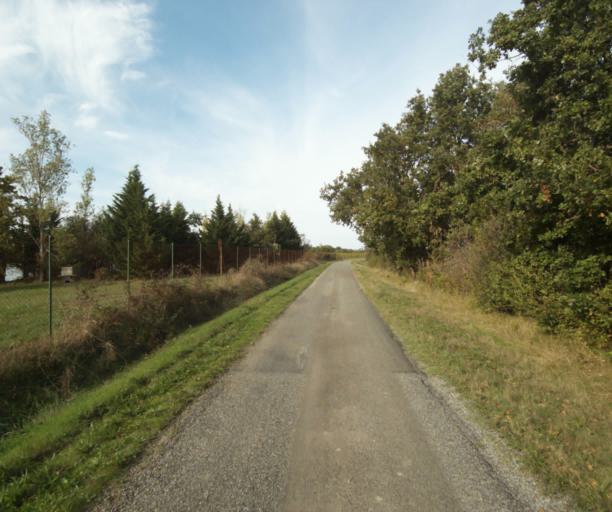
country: FR
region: Midi-Pyrenees
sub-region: Departement du Tarn-et-Garonne
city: Campsas
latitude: 43.9173
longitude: 1.3230
